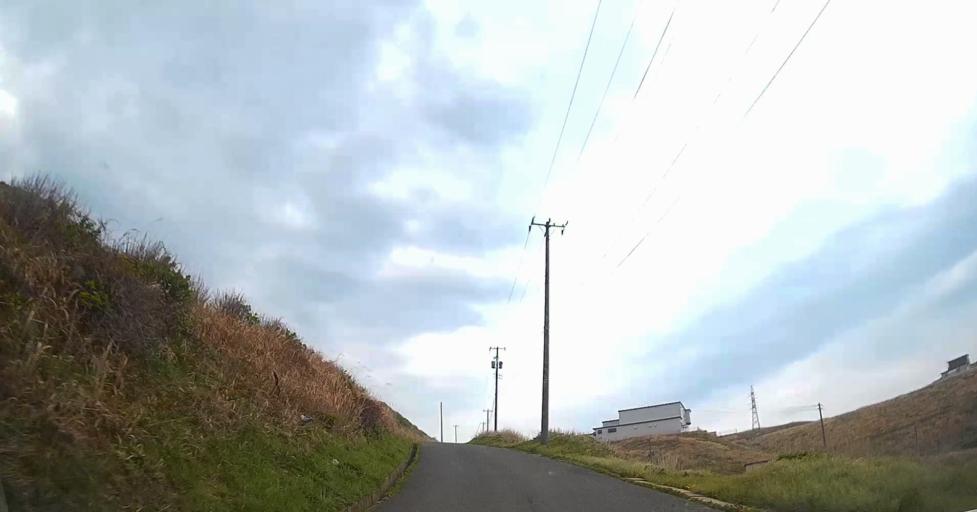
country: JP
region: Aomori
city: Shimokizukuri
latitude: 41.2533
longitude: 140.3426
